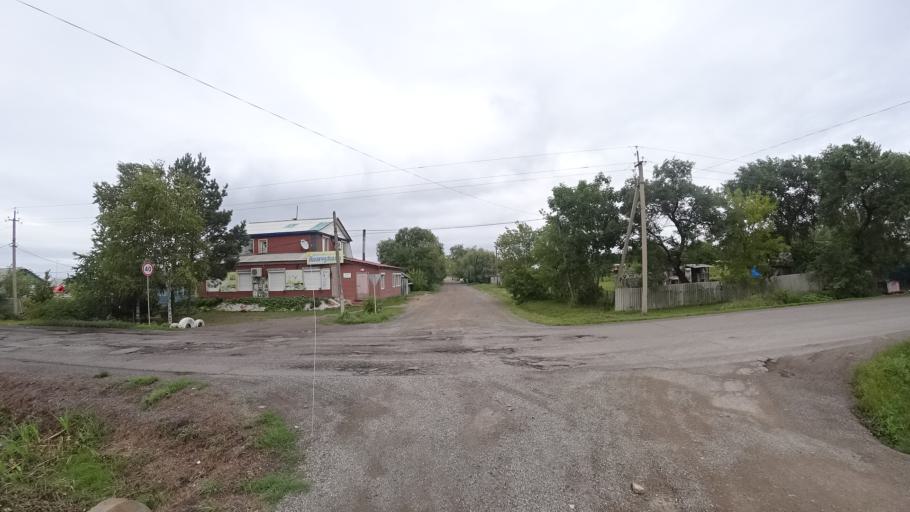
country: RU
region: Primorskiy
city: Chernigovka
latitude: 44.3432
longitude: 132.5665
